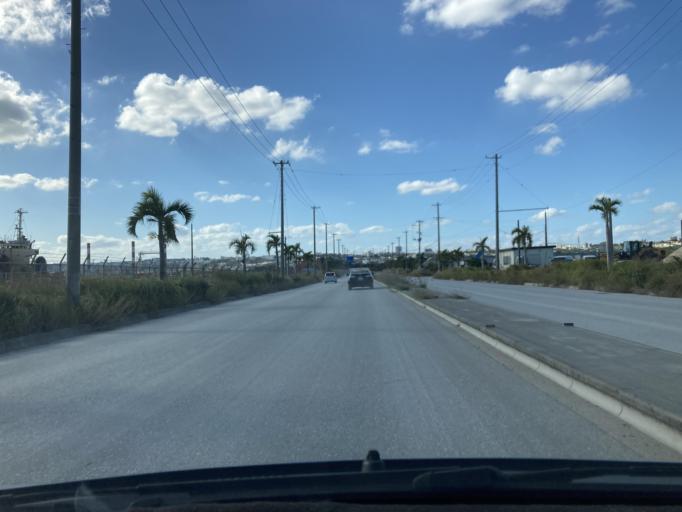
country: JP
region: Okinawa
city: Katsuren-haebaru
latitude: 26.3269
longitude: 127.8473
